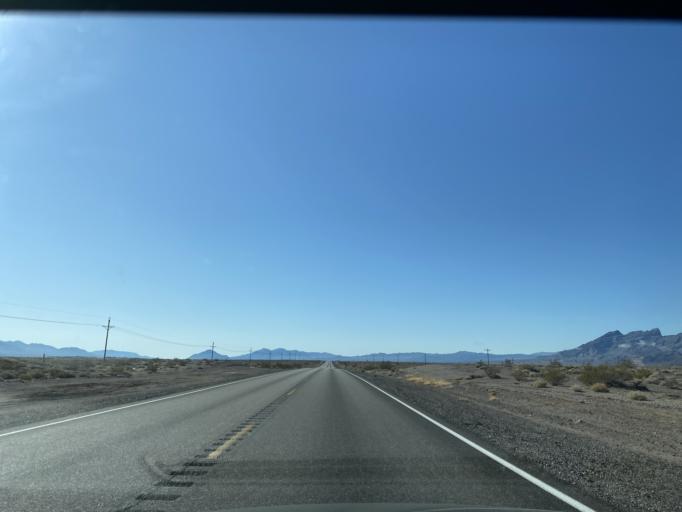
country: US
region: Nevada
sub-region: Nye County
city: Pahrump
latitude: 36.4560
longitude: -116.4218
